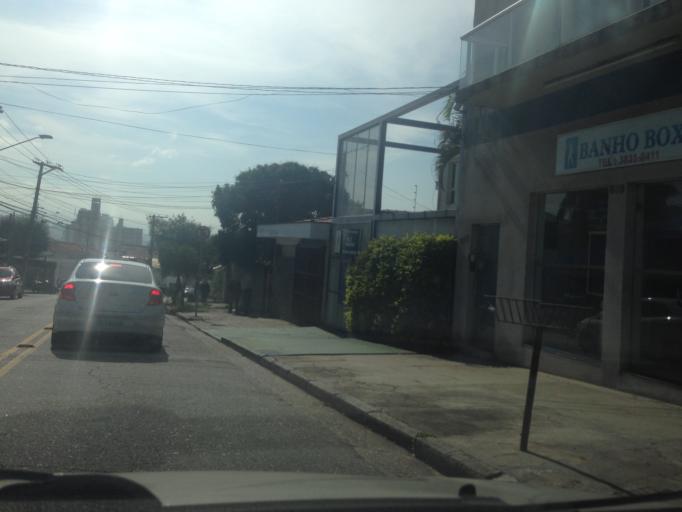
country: BR
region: Sao Paulo
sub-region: Sao Paulo
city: Sao Paulo
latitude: -23.5306
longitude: -46.7093
